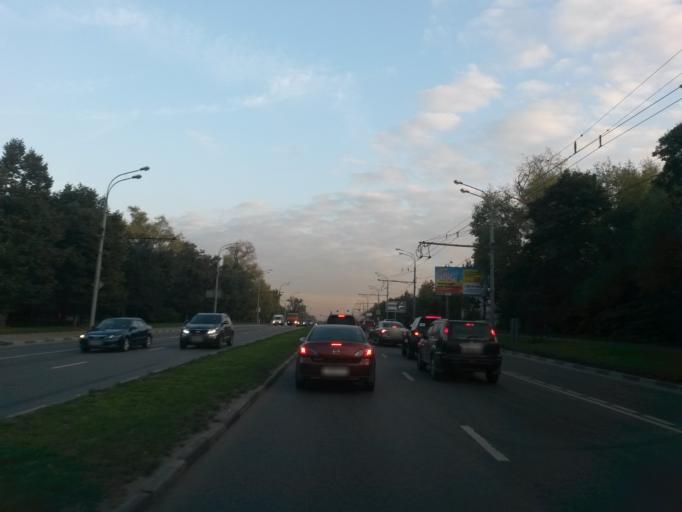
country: RU
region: Moscow
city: Tsaritsyno
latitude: 55.6117
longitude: 37.6628
